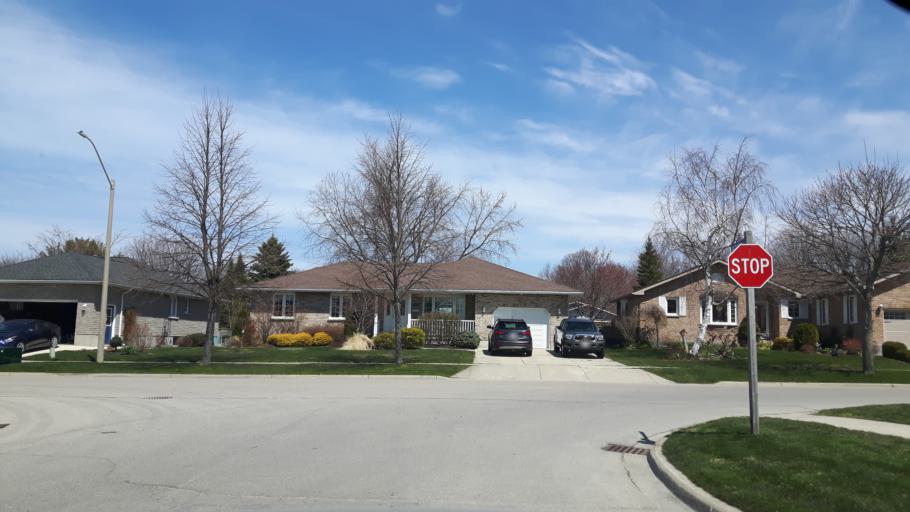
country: CA
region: Ontario
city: Goderich
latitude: 43.7292
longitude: -81.7174
